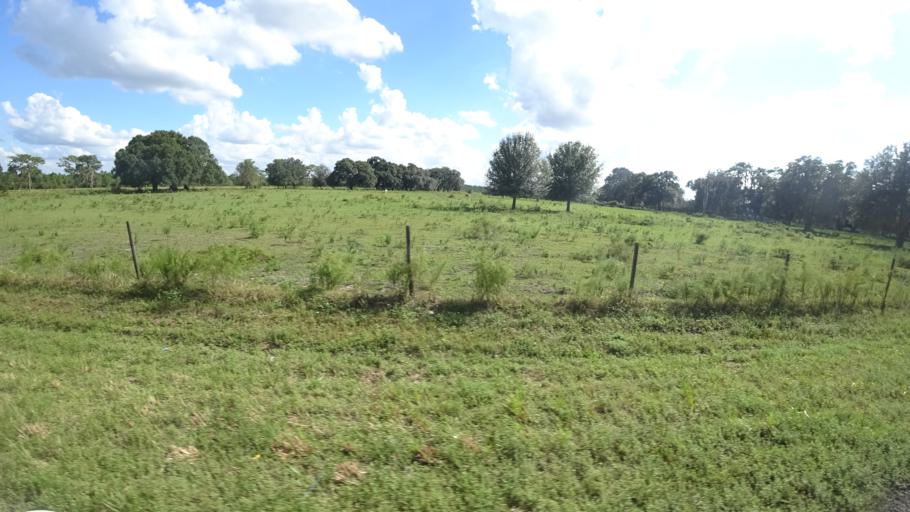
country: US
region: Florida
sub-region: Hardee County
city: Wauchula
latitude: 27.4509
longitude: -82.1018
